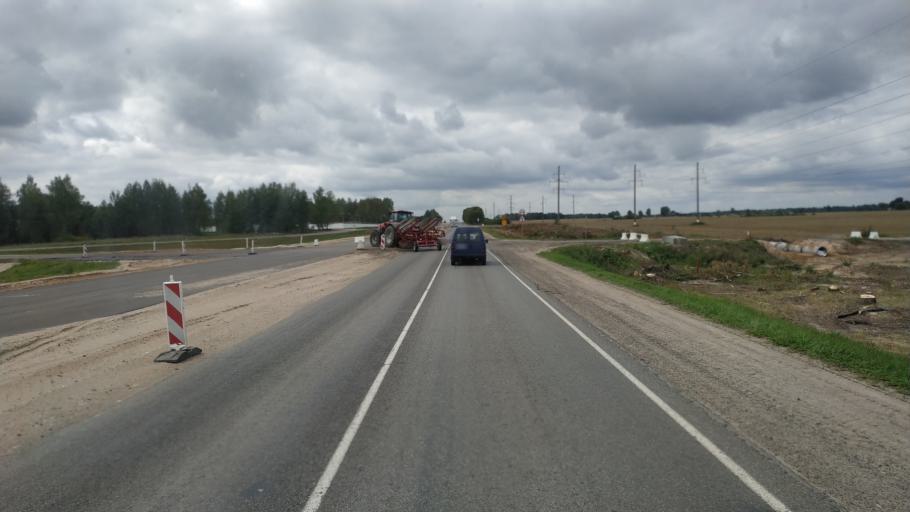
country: BY
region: Mogilev
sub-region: Mahilyowski Rayon
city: Kadino
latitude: 53.8680
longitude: 30.4721
